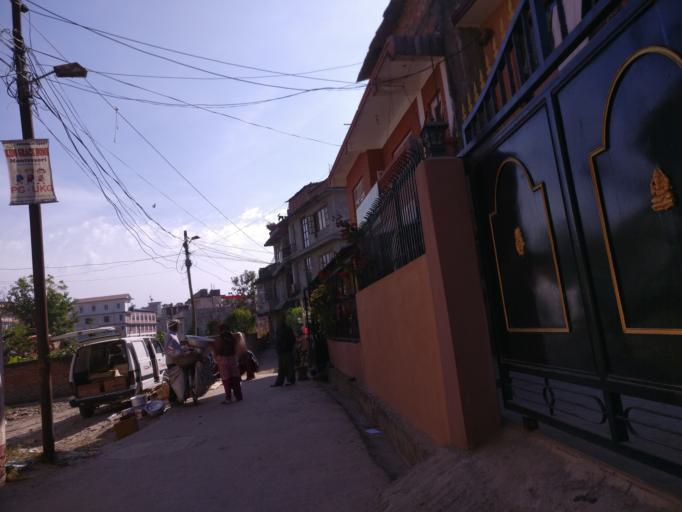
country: NP
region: Central Region
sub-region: Bagmati Zone
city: Patan
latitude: 27.6585
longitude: 85.3156
